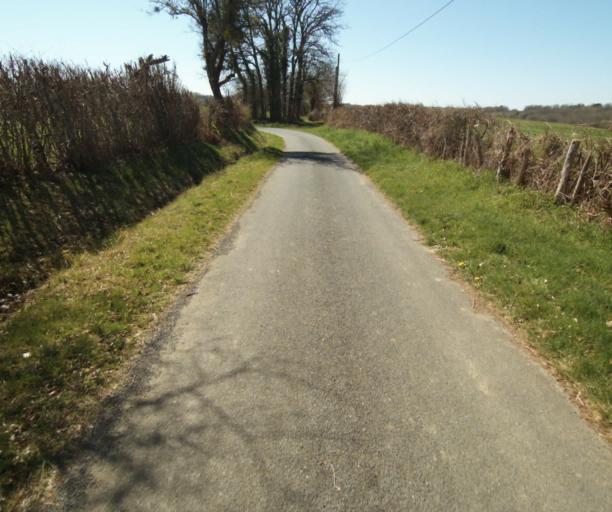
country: FR
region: Limousin
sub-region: Departement de la Correze
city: Chamboulive
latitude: 45.4331
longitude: 1.6850
